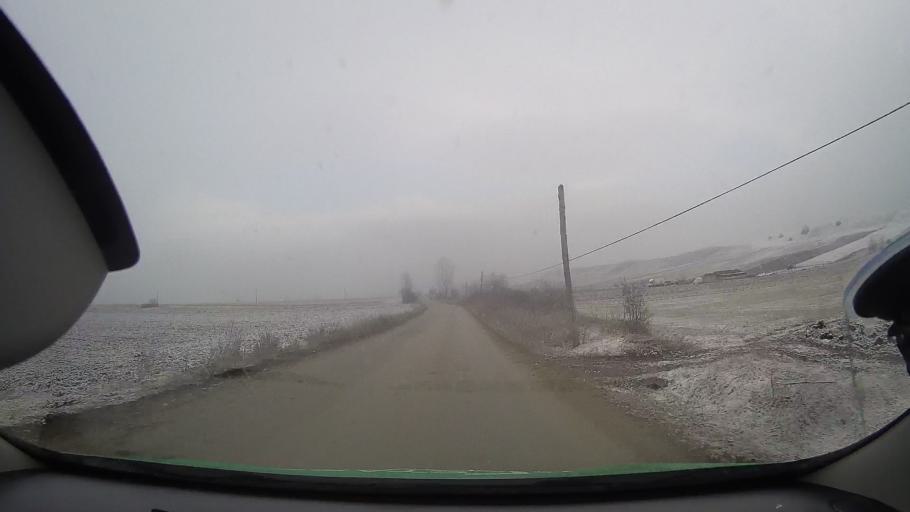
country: RO
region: Alba
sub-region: Oras Ocna Mures
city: Razboieni-Cetate
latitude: 46.3923
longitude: 23.8959
